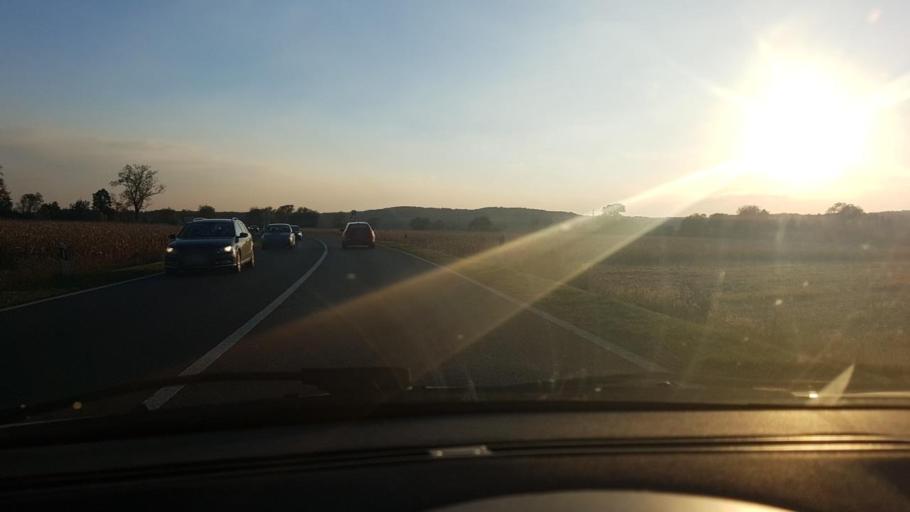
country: HR
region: Zagrebacka
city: Pojatno
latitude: 45.9081
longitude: 15.8133
